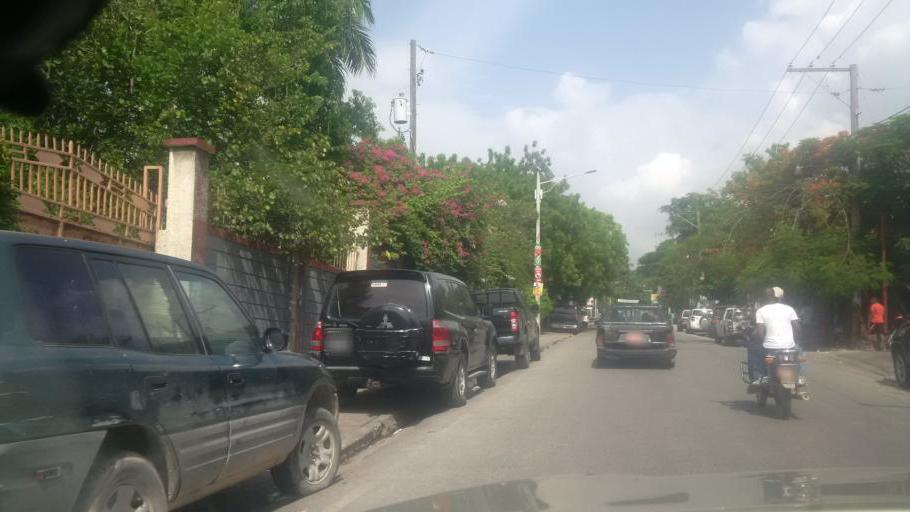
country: HT
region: Ouest
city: Port-au-Prince
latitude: 18.5333
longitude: -72.3265
